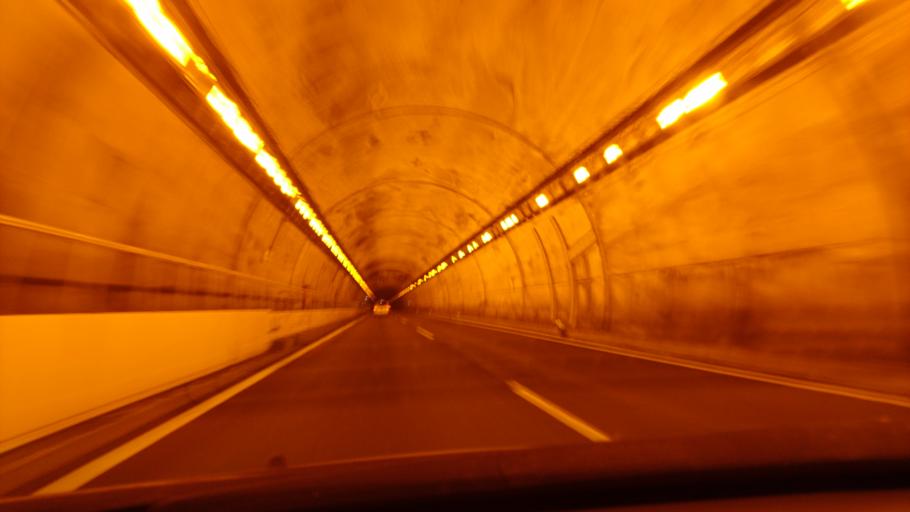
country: JP
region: Akita
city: Hanawa
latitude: 40.0190
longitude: 140.9854
